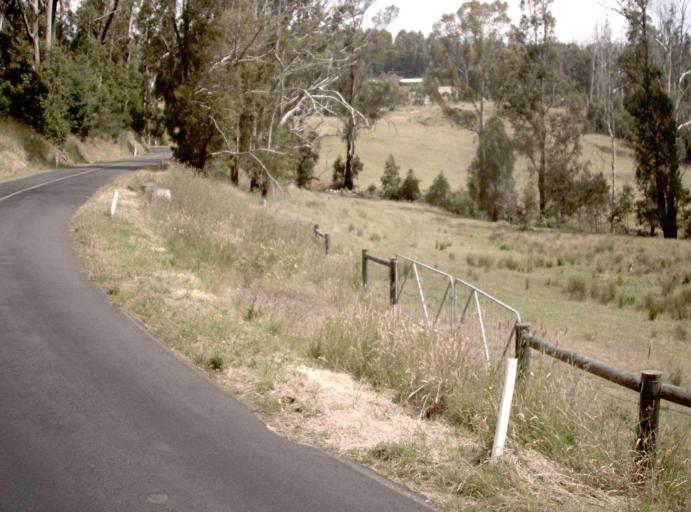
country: AU
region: Victoria
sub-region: Latrobe
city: Traralgon
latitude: -38.3279
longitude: 146.5748
